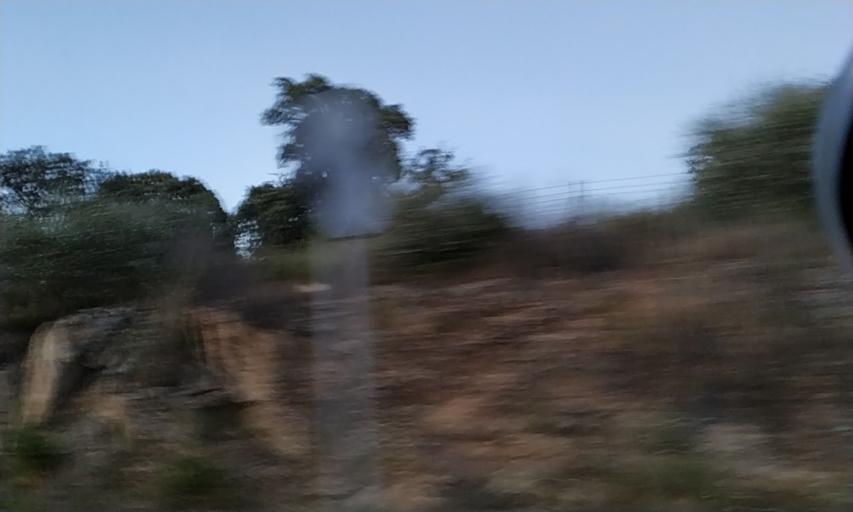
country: ES
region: Extremadura
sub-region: Provincia de Caceres
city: Piedras Albas
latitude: 39.7619
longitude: -6.9068
